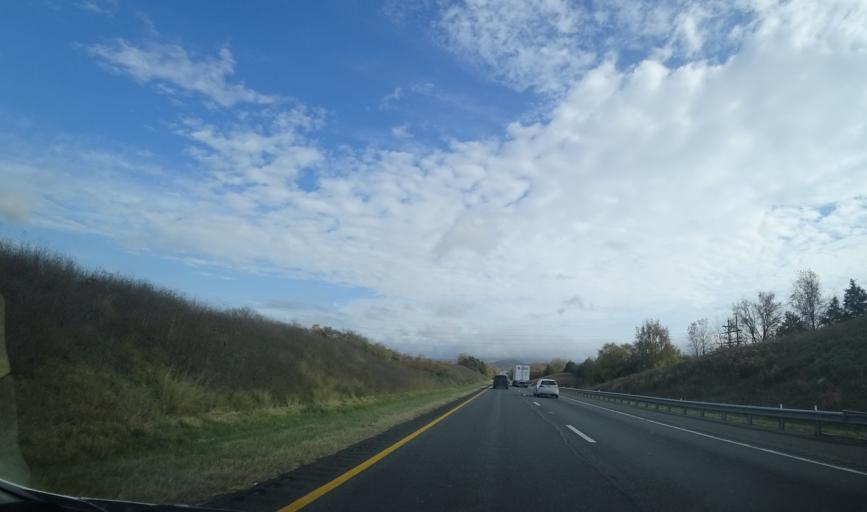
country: US
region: Virginia
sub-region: Warren County
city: Front Royal
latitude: 38.9501
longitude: -78.1696
